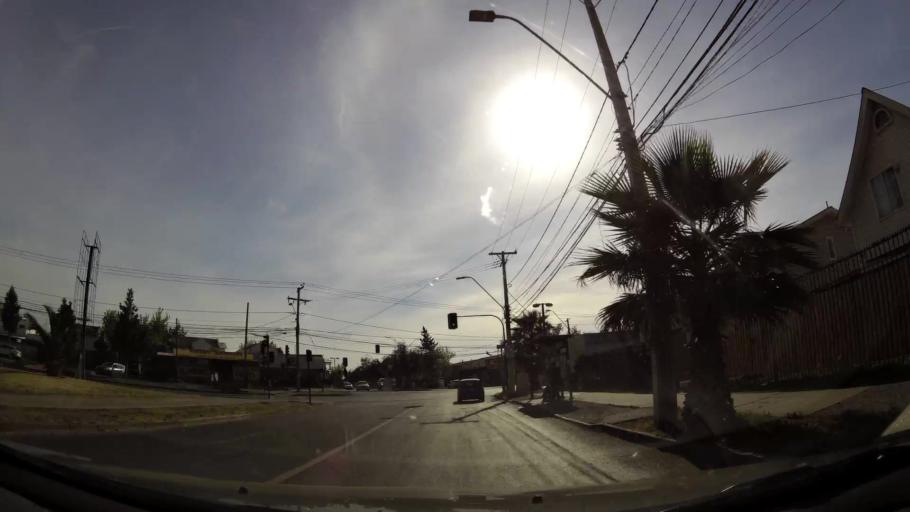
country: CL
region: Santiago Metropolitan
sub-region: Provincia de Cordillera
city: Puente Alto
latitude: -33.5925
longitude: -70.5600
